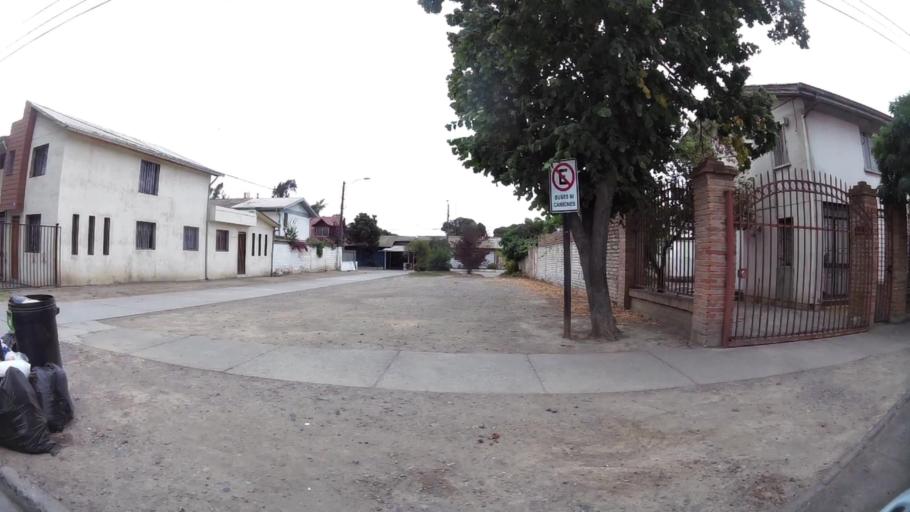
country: CL
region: O'Higgins
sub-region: Provincia de Cachapoal
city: Rancagua
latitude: -34.1599
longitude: -70.7436
